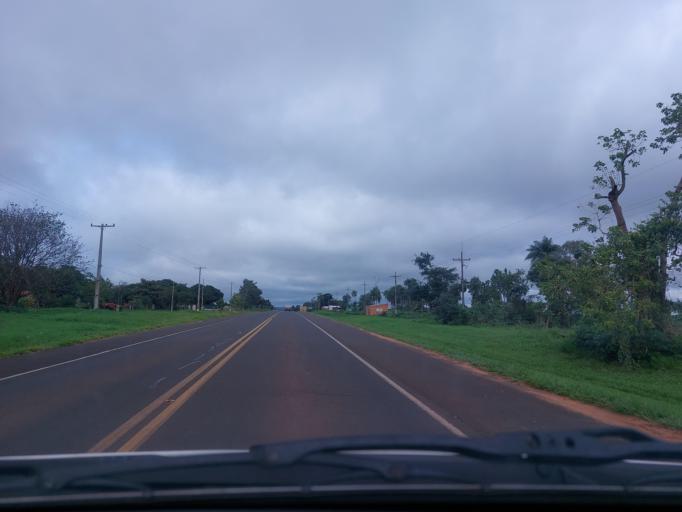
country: PY
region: San Pedro
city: Guayaybi
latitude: -24.6093
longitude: -56.3822
